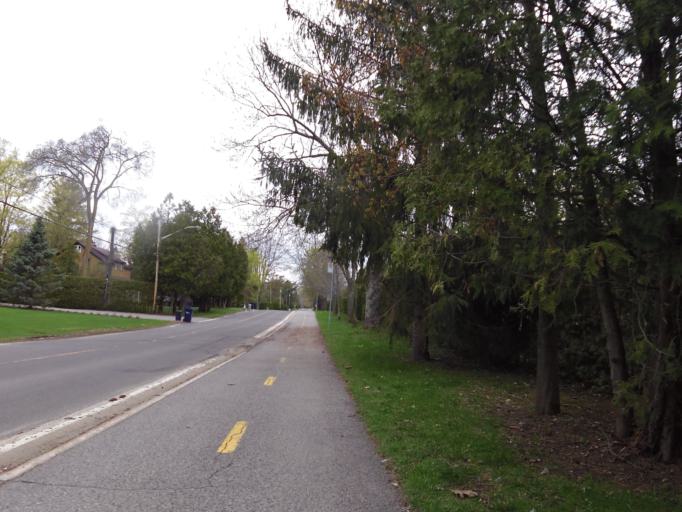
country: CA
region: Quebec
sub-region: Laurentides
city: Deux-Montagnes
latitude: 45.5263
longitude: -73.8760
